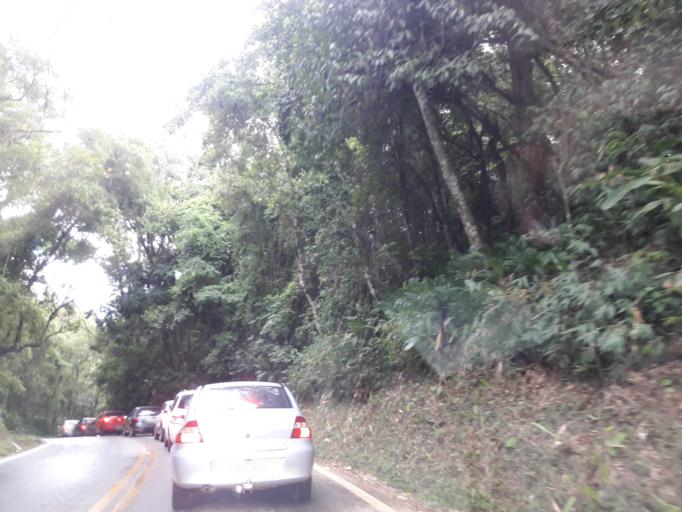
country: BR
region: Sao Paulo
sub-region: Aruja
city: Aruja
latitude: -23.3375
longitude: -46.4351
